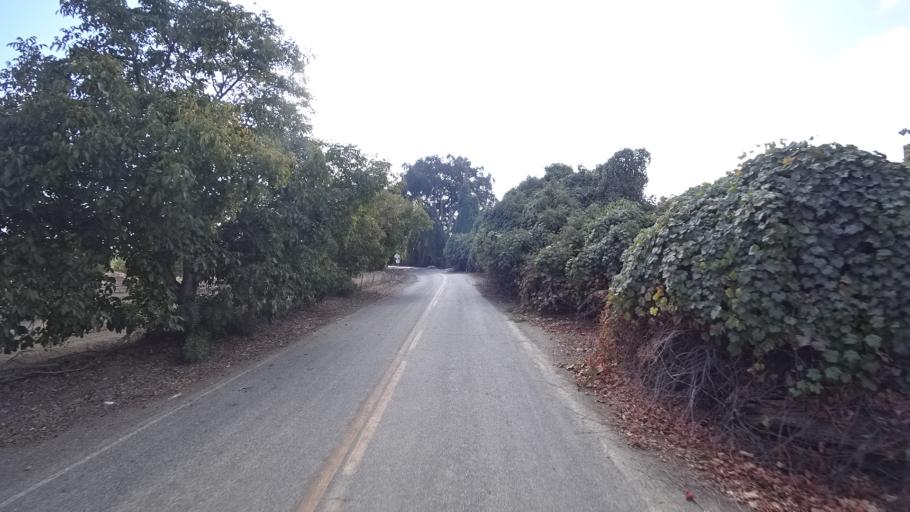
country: US
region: California
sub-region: Yolo County
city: Woodland
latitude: 38.7596
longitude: -121.6779
